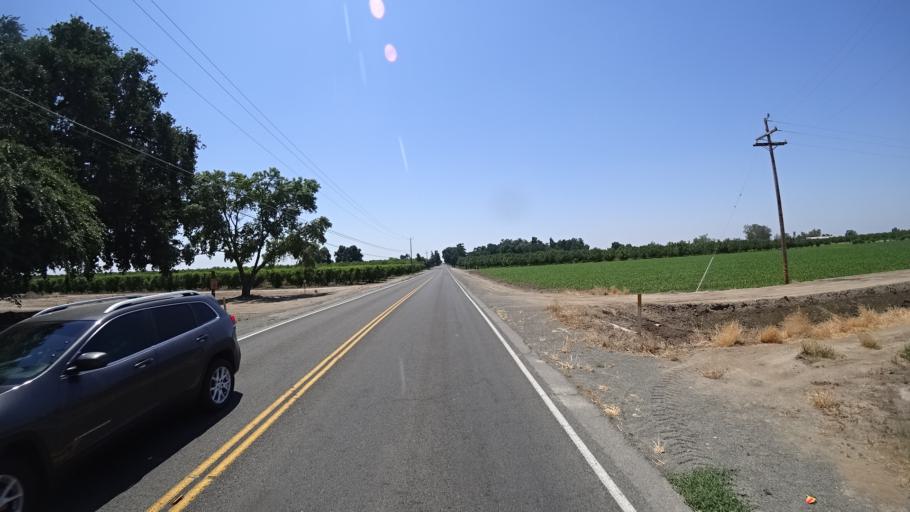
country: US
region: California
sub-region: Fresno County
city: Laton
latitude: 36.4159
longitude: -119.6864
